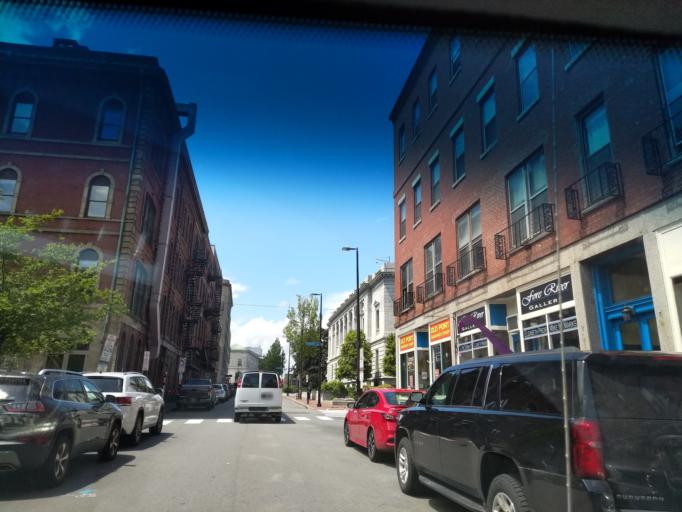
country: US
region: Maine
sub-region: Cumberland County
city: Portland
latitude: 43.6582
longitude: -70.2547
